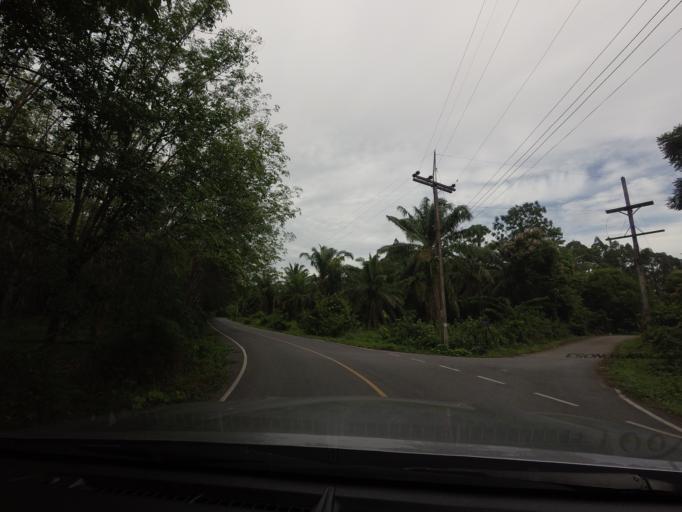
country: TH
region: Nakhon Si Thammarat
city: Phra Phrom
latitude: 8.2811
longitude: 99.9405
